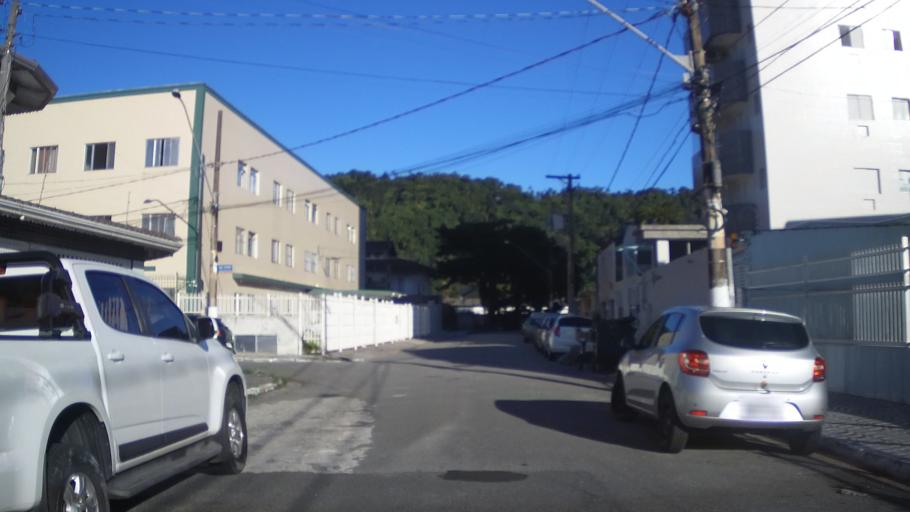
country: BR
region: Sao Paulo
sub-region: Praia Grande
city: Praia Grande
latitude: -24.0126
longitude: -46.3967
